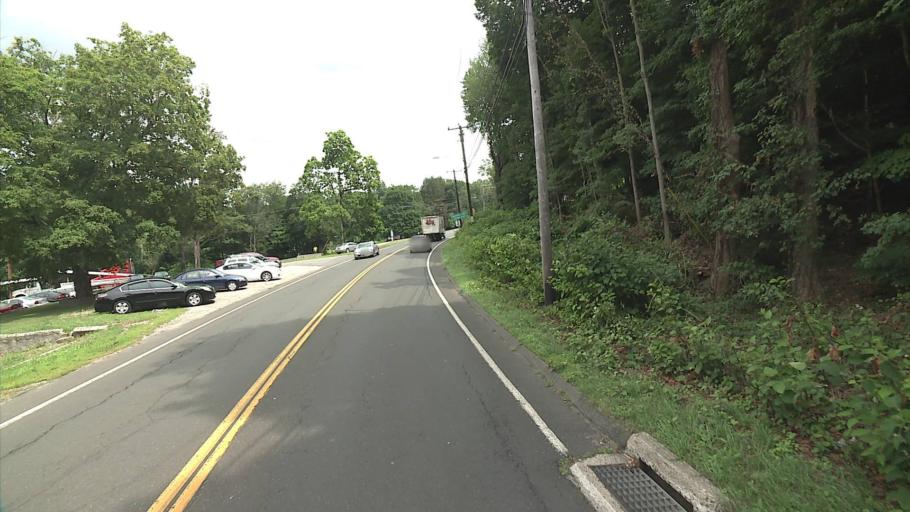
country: US
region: Connecticut
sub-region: New Haven County
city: Seymour
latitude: 41.3985
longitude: -73.0520
